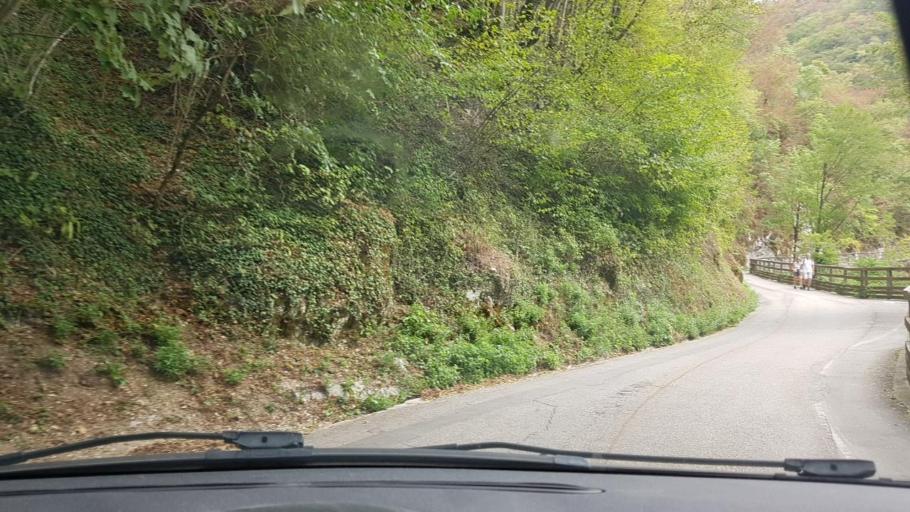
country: SI
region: Tolmin
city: Tolmin
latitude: 46.2017
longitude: 13.7417
